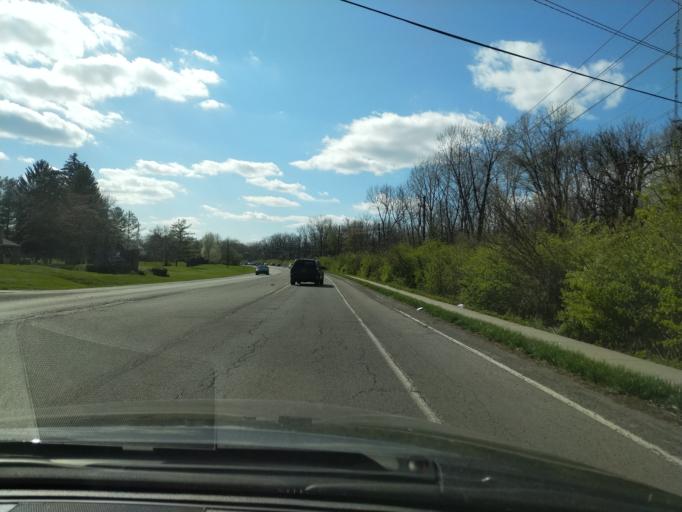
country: US
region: Indiana
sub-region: Marion County
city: Meridian Hills
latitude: 39.8863
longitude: -86.2000
